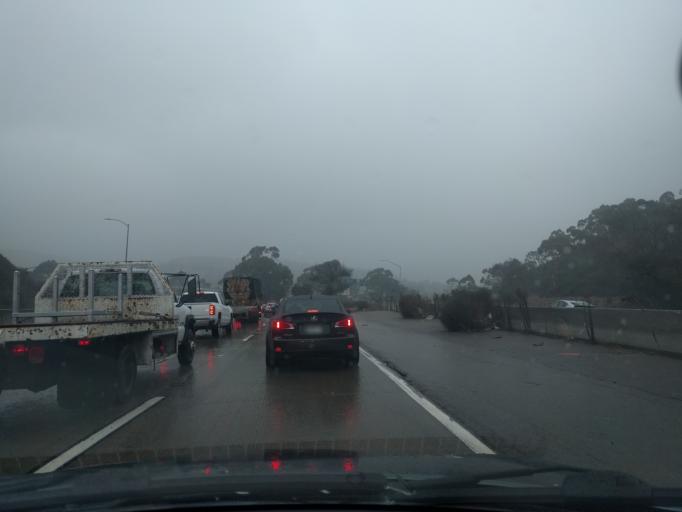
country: US
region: California
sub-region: San Diego County
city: San Diego
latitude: 32.7745
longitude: -117.1118
